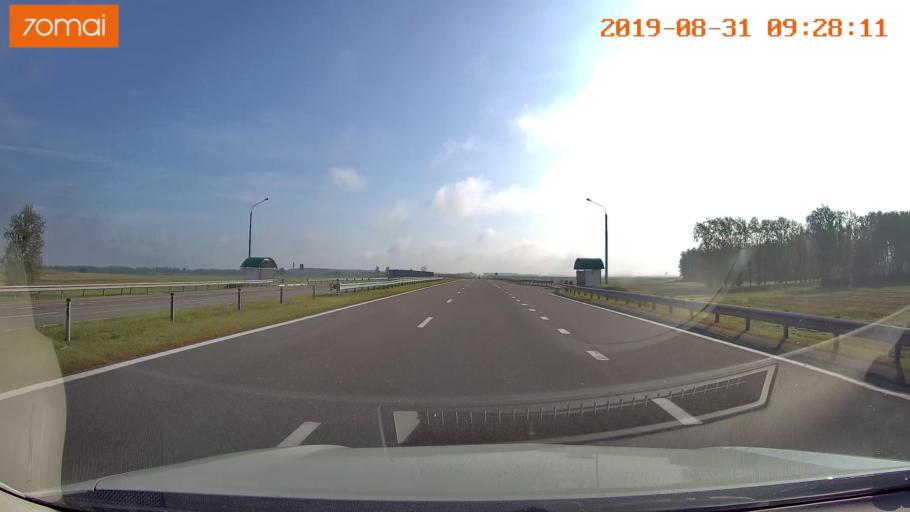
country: BY
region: Minsk
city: Byerazino
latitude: 53.8403
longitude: 29.0561
